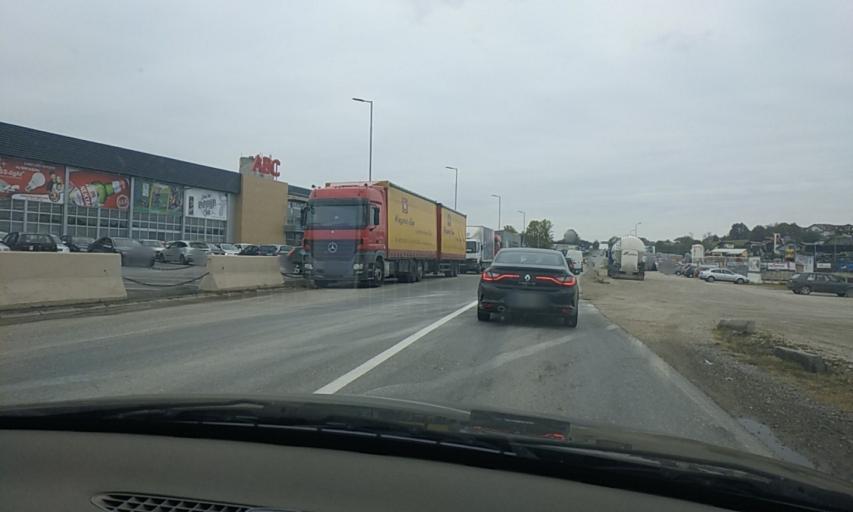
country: BA
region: Republika Srpska
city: Prnjavor
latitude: 44.8561
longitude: 17.6805
